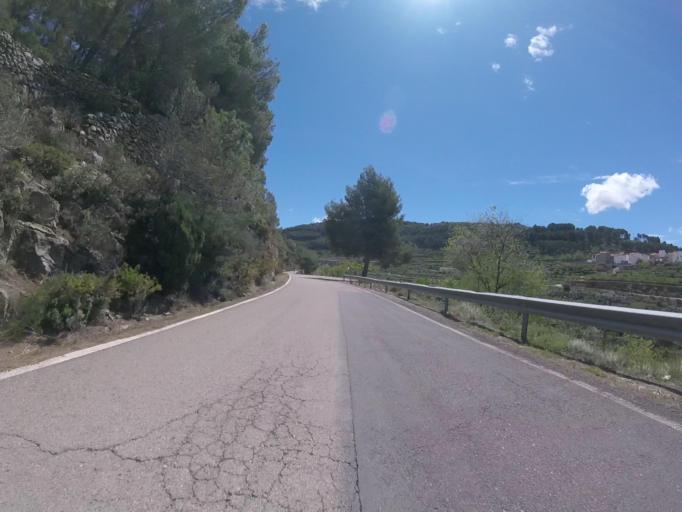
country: ES
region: Valencia
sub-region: Provincia de Castello
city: Sierra-Engarceran
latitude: 40.2732
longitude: -0.0188
